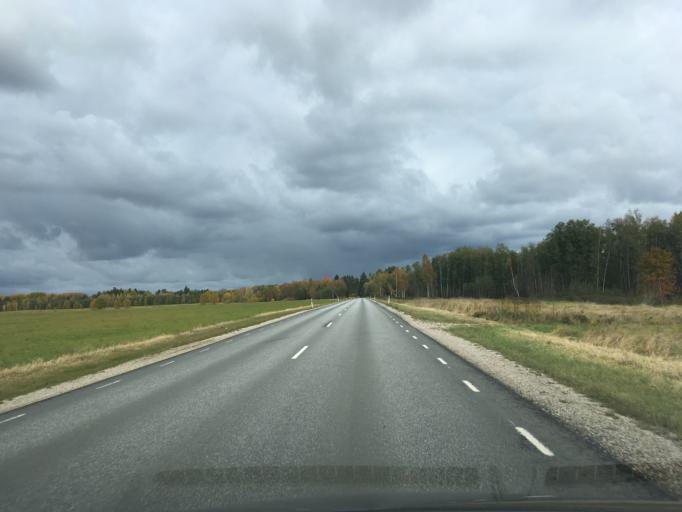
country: EE
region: Harju
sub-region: Anija vald
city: Kehra
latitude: 59.2864
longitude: 25.3748
